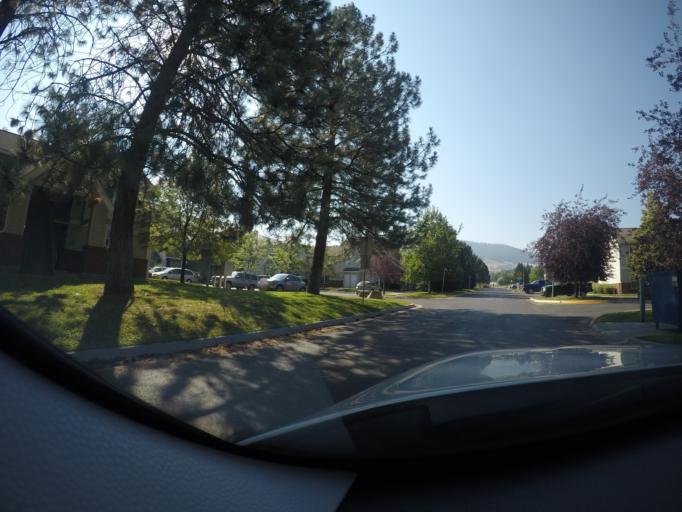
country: US
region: Montana
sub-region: Missoula County
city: Missoula
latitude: 46.8456
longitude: -113.9933
